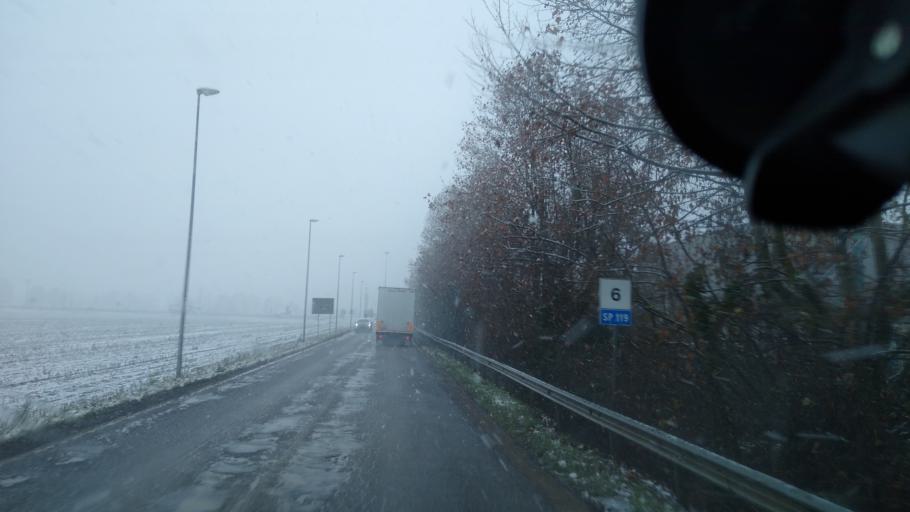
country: IT
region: Lombardy
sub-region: Provincia di Bergamo
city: Spirano
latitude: 45.5957
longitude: 9.6655
